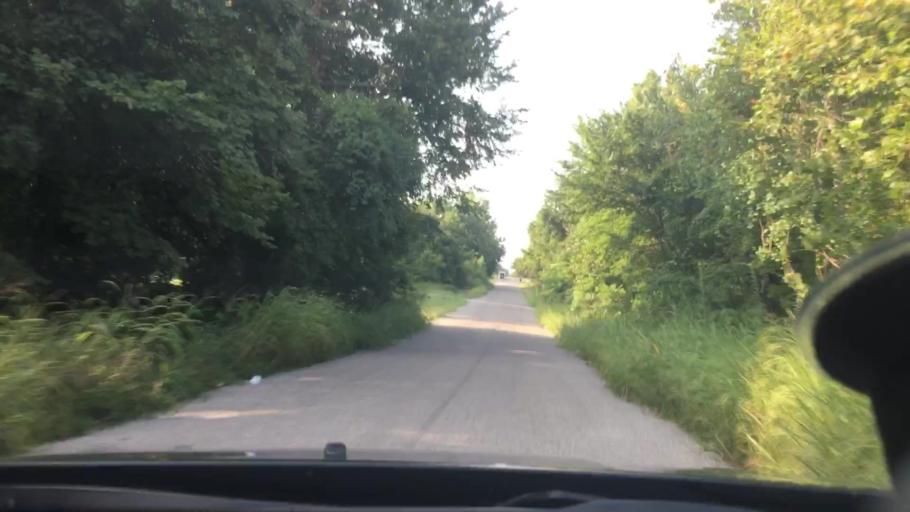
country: US
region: Oklahoma
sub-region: Pontotoc County
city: Ada
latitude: 34.7914
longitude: -96.7397
